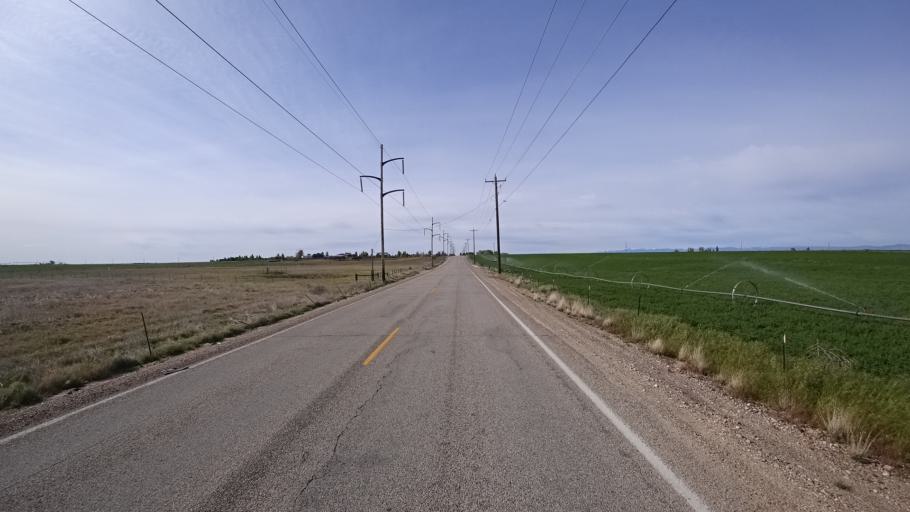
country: US
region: Idaho
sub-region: Ada County
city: Kuna
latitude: 43.4655
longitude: -116.3345
